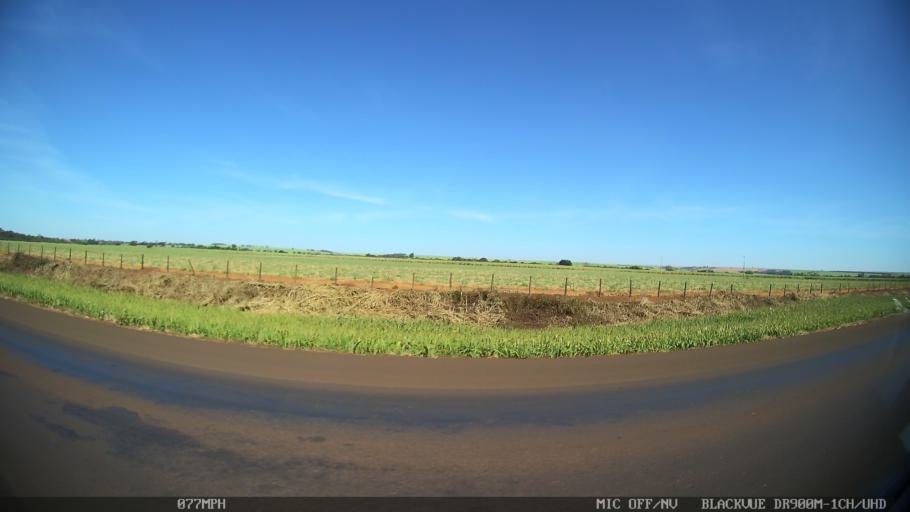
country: BR
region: Sao Paulo
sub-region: Ipua
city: Ipua
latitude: -20.5032
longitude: -47.9409
